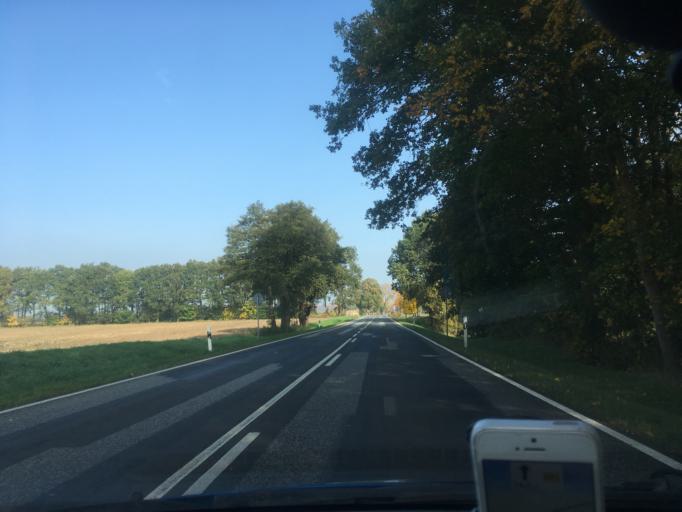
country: DE
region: Mecklenburg-Vorpommern
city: Hagenow
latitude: 53.4587
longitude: 11.2234
